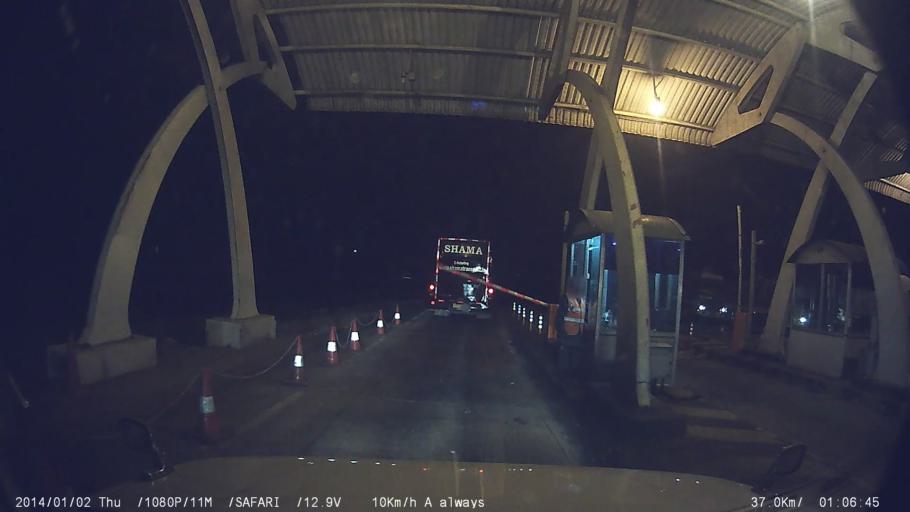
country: IN
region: Tamil Nadu
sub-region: Coimbatore
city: Madukkarai
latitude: 10.9212
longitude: 76.9892
